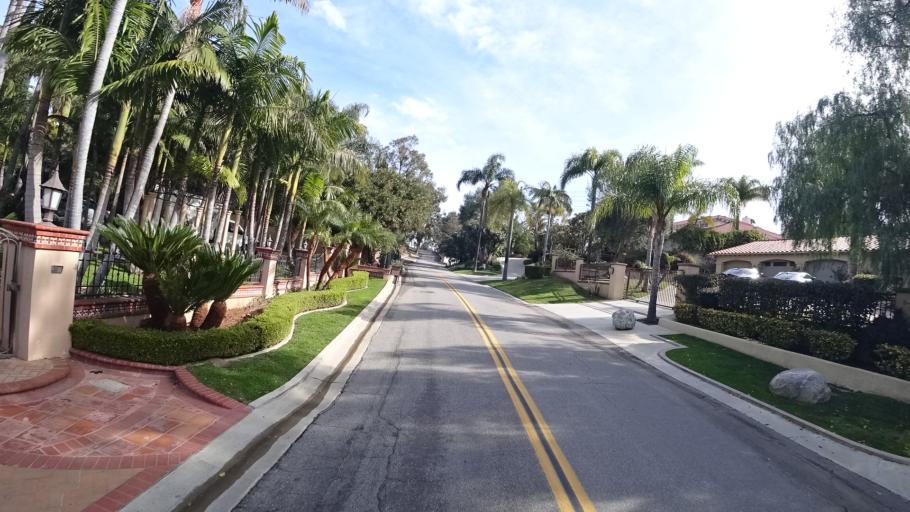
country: US
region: California
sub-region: Orange County
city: Yorba Linda
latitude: 33.8524
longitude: -117.7570
